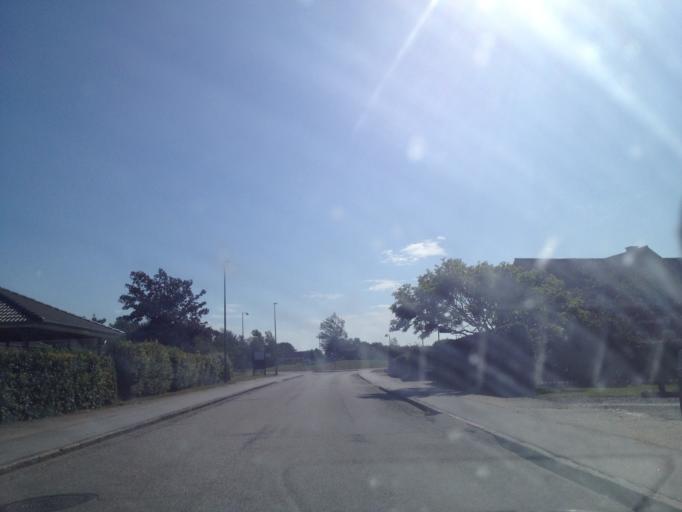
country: DK
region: South Denmark
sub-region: Haderslev Kommune
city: Vojens
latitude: 55.3114
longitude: 9.2829
